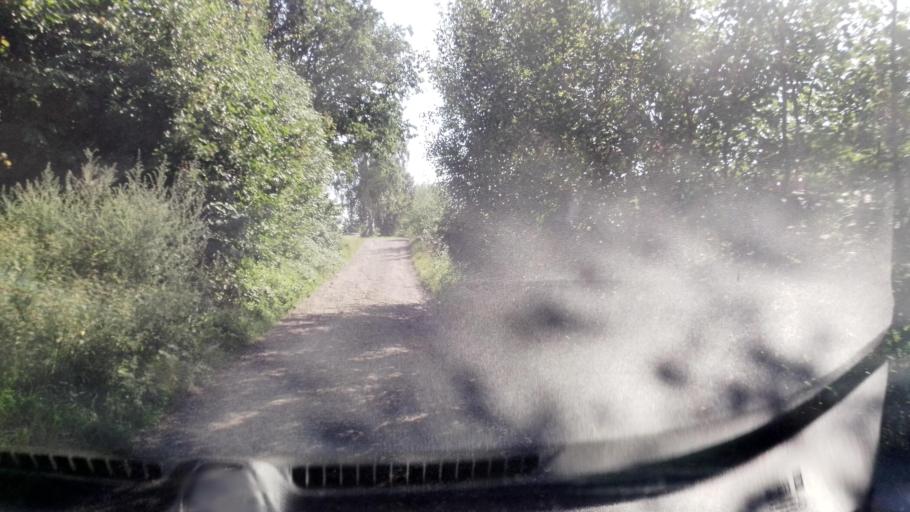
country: NL
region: Limburg
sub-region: Gemeente Voerendaal
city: Klimmen
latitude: 50.8893
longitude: 5.8709
